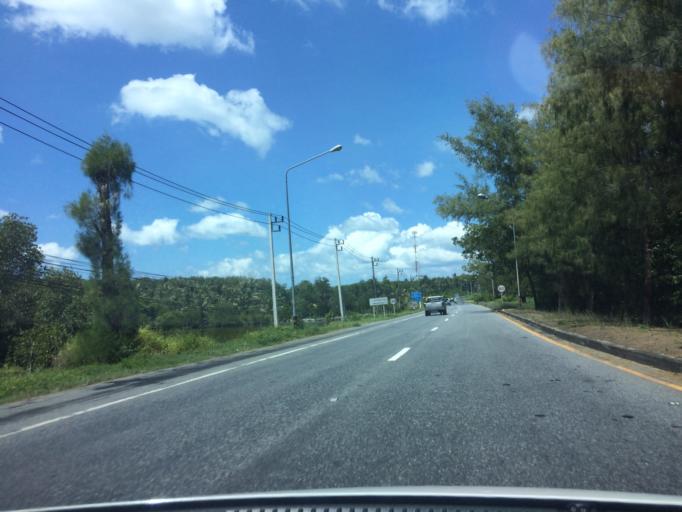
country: TH
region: Phuket
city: Thalang
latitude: 8.2104
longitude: 98.2984
